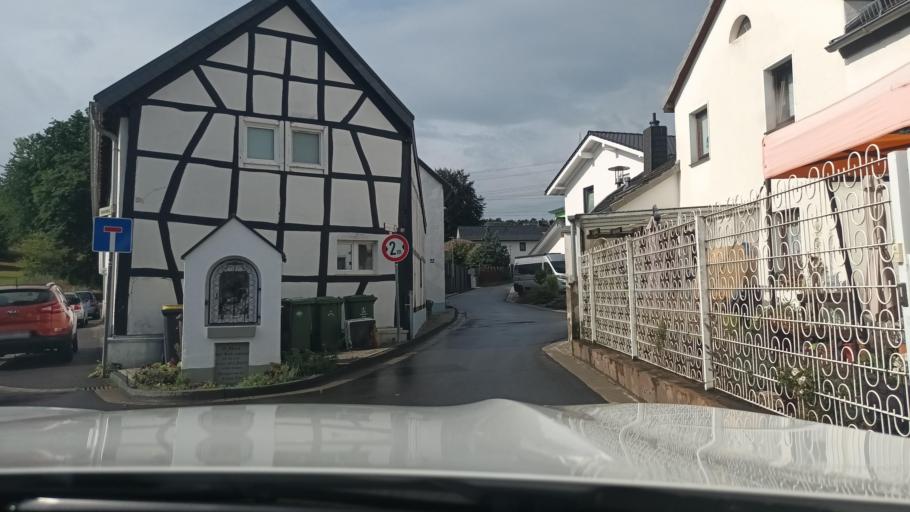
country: DE
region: North Rhine-Westphalia
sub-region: Regierungsbezirk Koln
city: Stossdorf
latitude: 50.7703
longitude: 7.2596
